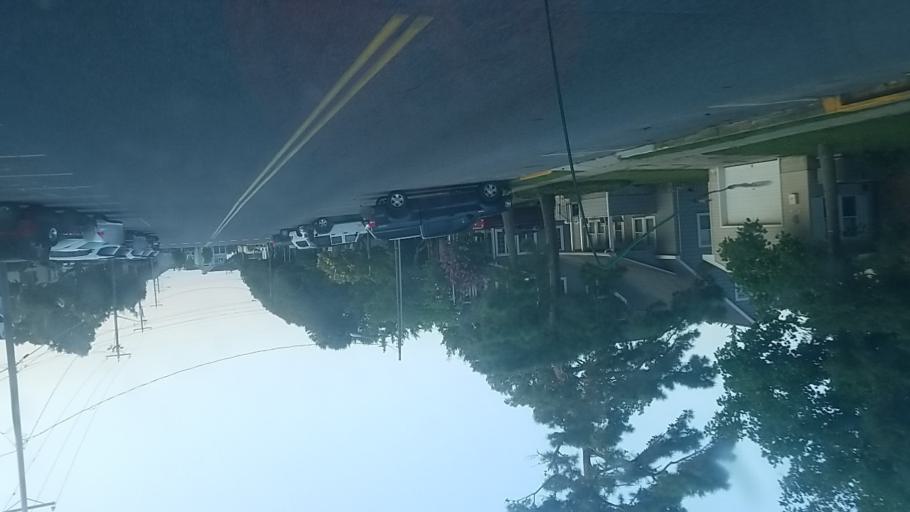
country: US
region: Delaware
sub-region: Sussex County
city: Rehoboth Beach
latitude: 38.7116
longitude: -75.0781
